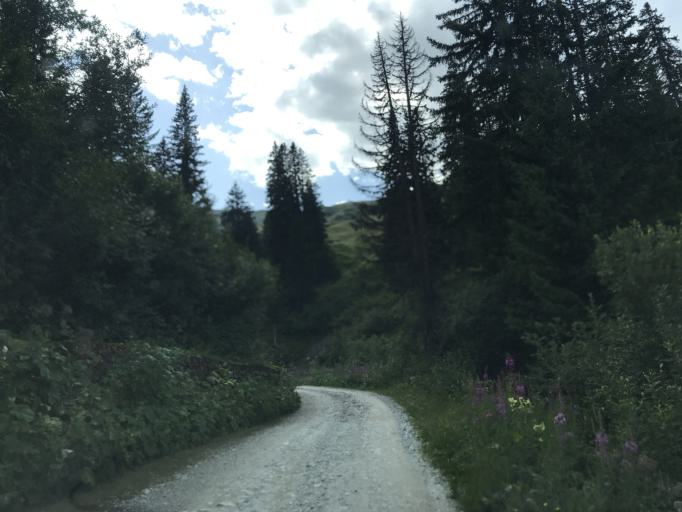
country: FR
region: Rhone-Alpes
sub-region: Departement de la Savoie
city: Beaufort
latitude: 45.6660
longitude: 6.6149
